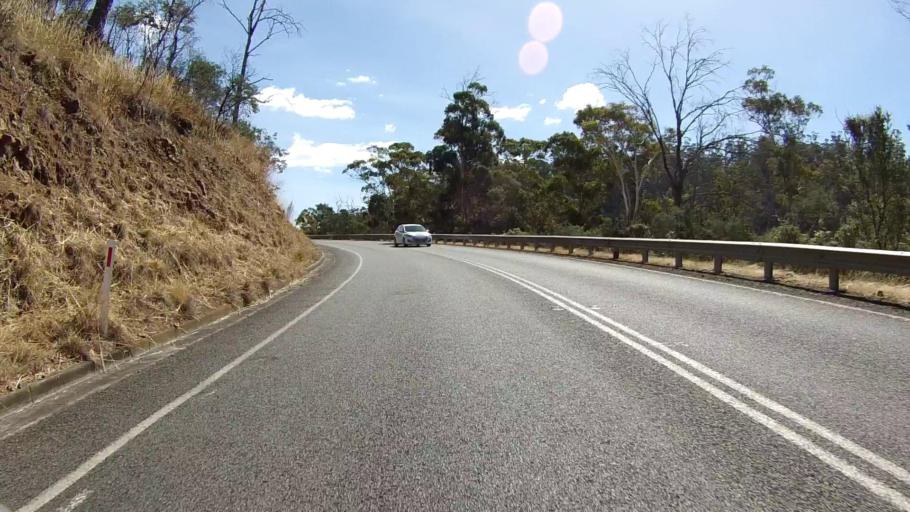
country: AU
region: Tasmania
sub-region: Sorell
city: Sorell
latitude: -42.6075
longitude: 147.6548
